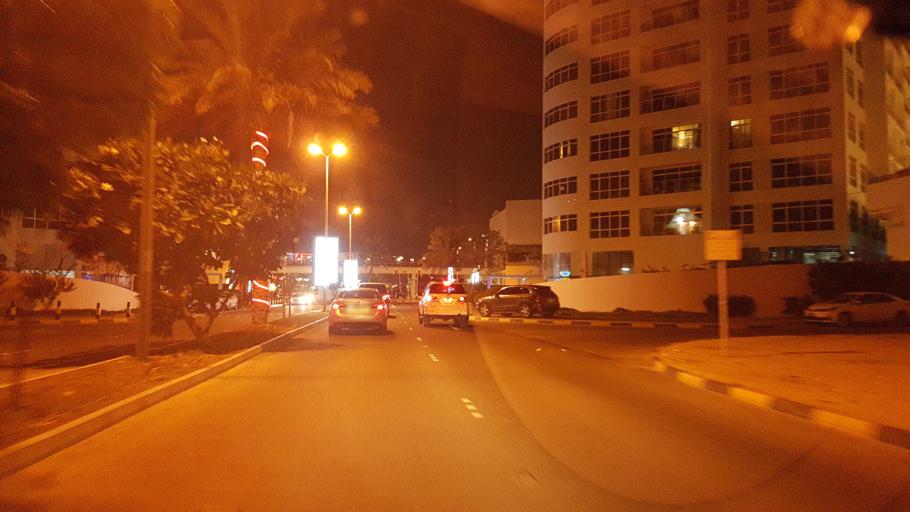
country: BH
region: Muharraq
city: Al Hadd
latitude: 26.2913
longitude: 50.6650
